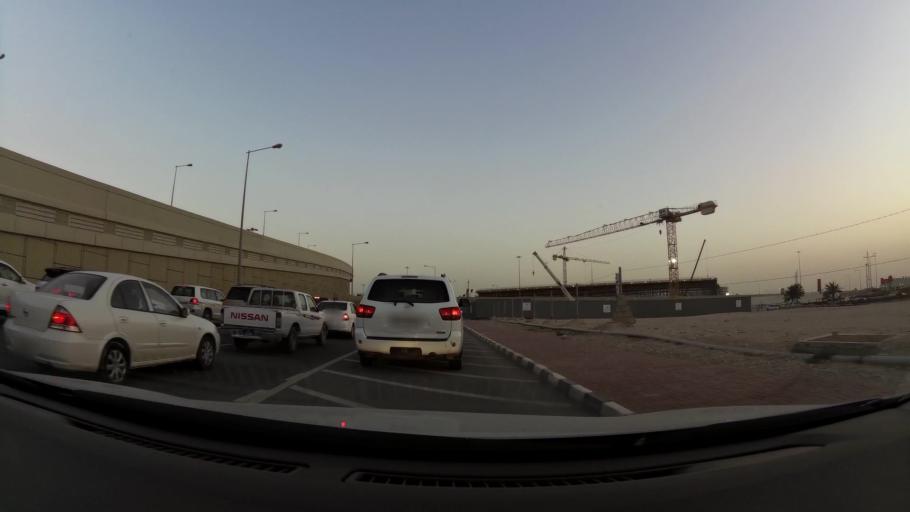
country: QA
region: Baladiyat ar Rayyan
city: Ar Rayyan
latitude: 25.2974
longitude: 51.4742
